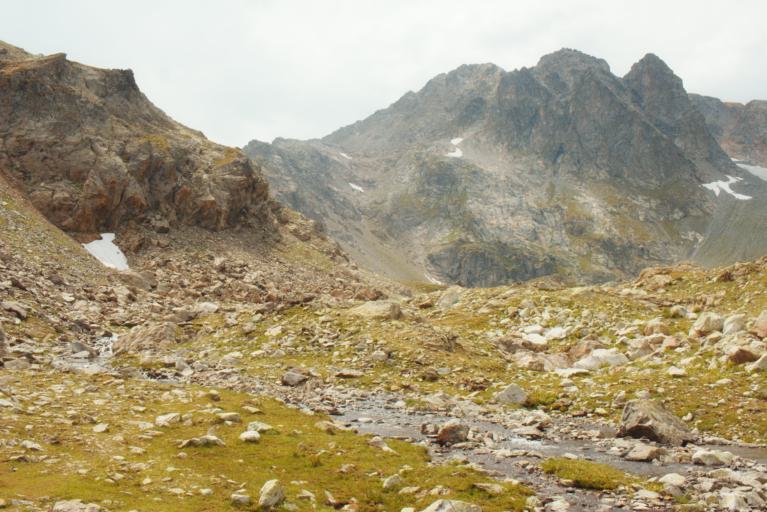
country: RU
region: Karachayevo-Cherkesiya
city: Nizhniy Arkhyz
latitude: 43.4512
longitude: 41.2360
